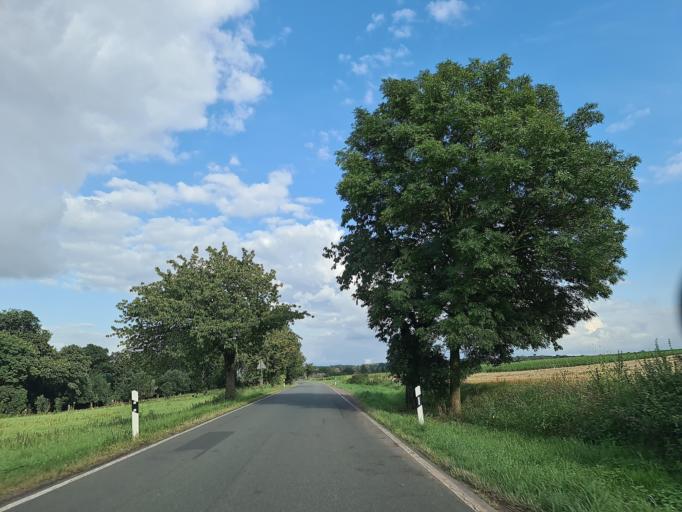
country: DE
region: Saxony-Anhalt
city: Droyssig
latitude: 51.0406
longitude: 11.9983
